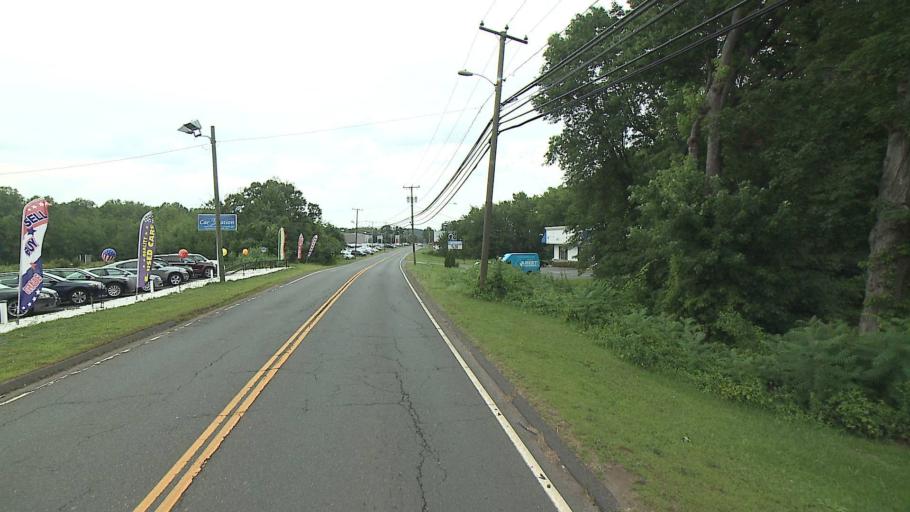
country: US
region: Connecticut
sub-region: Middlesex County
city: Cromwell
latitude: 41.5879
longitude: -72.6752
